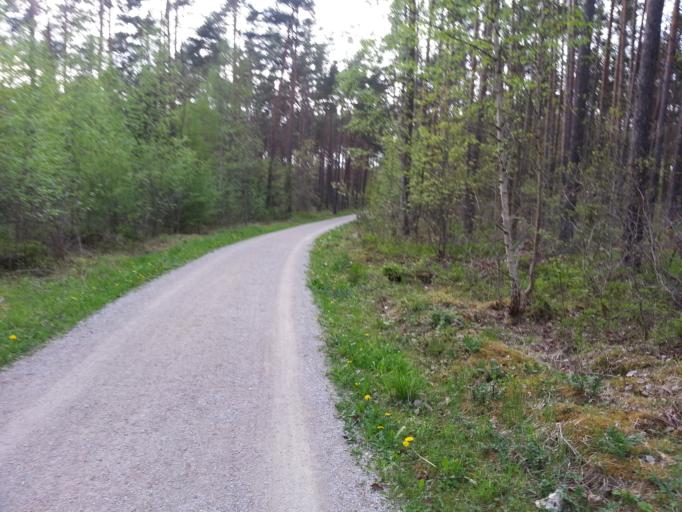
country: DE
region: Bavaria
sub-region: Regierungsbezirk Mittelfranken
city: Erlangen
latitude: 49.5692
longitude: 11.0253
